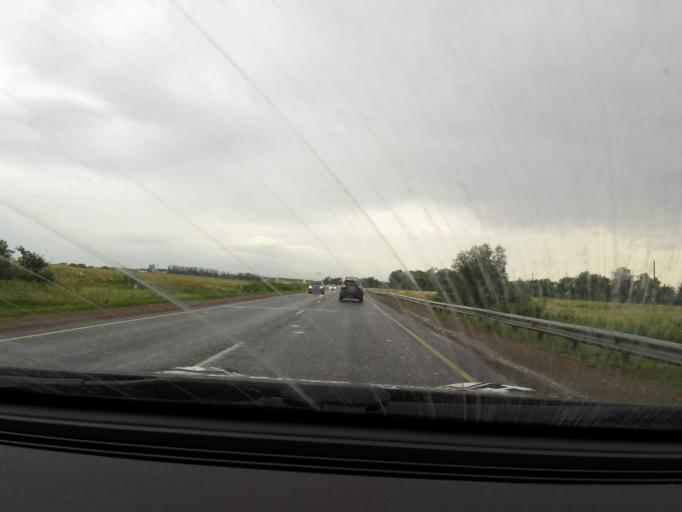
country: RU
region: Bashkortostan
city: Mikhaylovka
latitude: 54.8221
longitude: 55.8355
